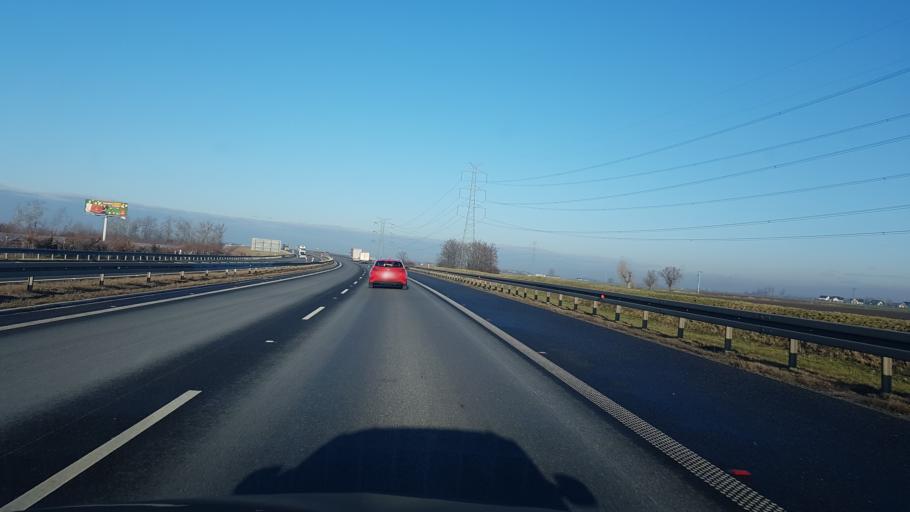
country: PL
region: Lower Silesian Voivodeship
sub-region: Powiat wroclawski
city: Zorawina
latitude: 50.9858
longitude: 17.0578
